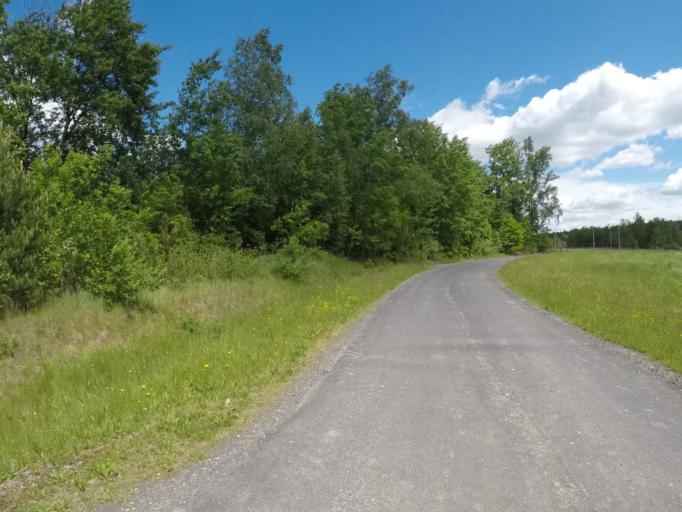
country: PL
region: Swietokrzyskie
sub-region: Powiat kielecki
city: Zagnansk
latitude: 50.9413
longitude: 20.6724
